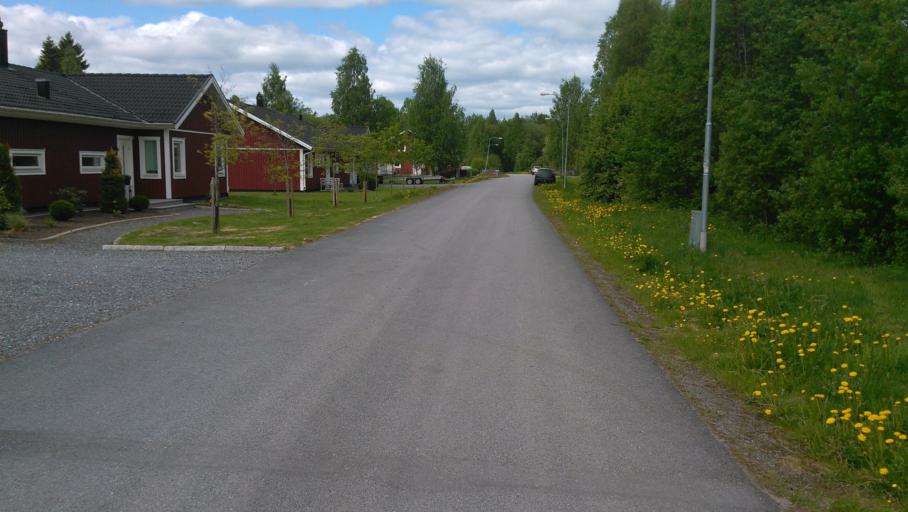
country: SE
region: Vaesterbotten
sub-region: Umea Kommun
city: Roback
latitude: 63.8767
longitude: 20.0542
